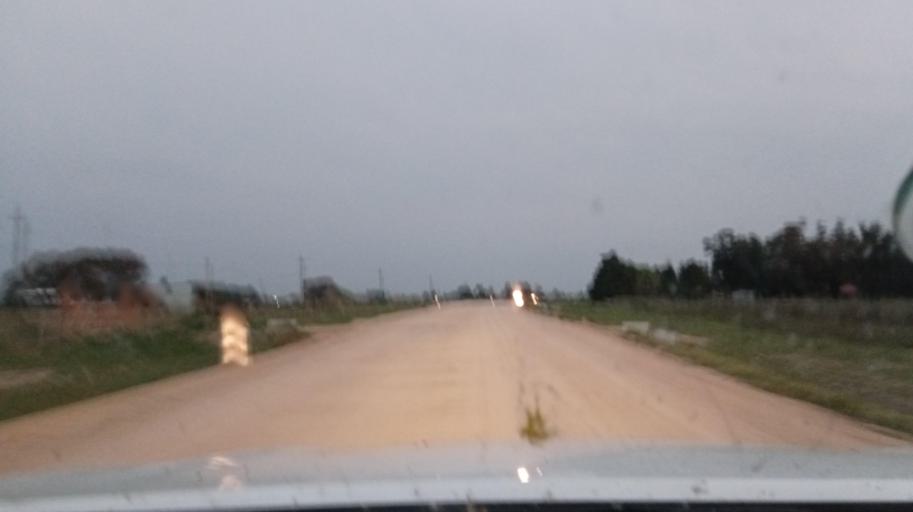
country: UY
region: Canelones
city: Santa Rosa
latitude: -34.5381
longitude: -56.0996
